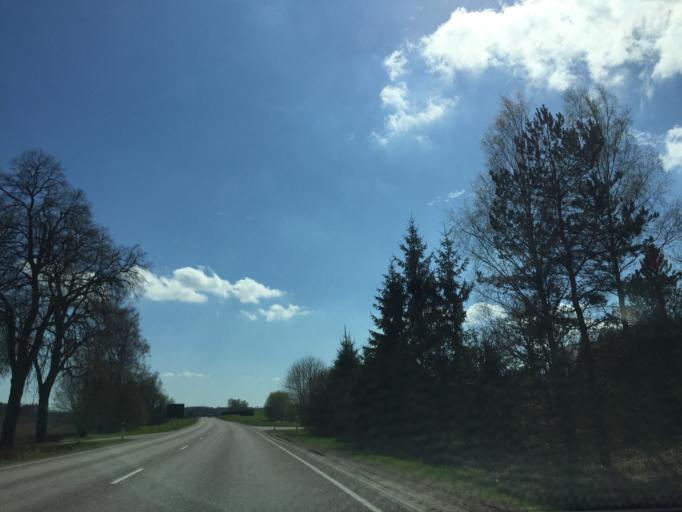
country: EE
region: Valgamaa
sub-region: Torva linn
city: Torva
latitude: 58.0526
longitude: 26.1930
